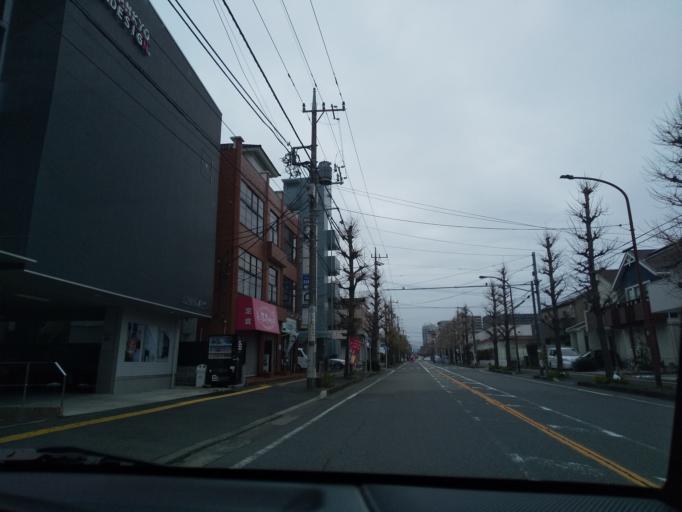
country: JP
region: Tokyo
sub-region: Machida-shi
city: Machida
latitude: 35.5657
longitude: 139.3777
